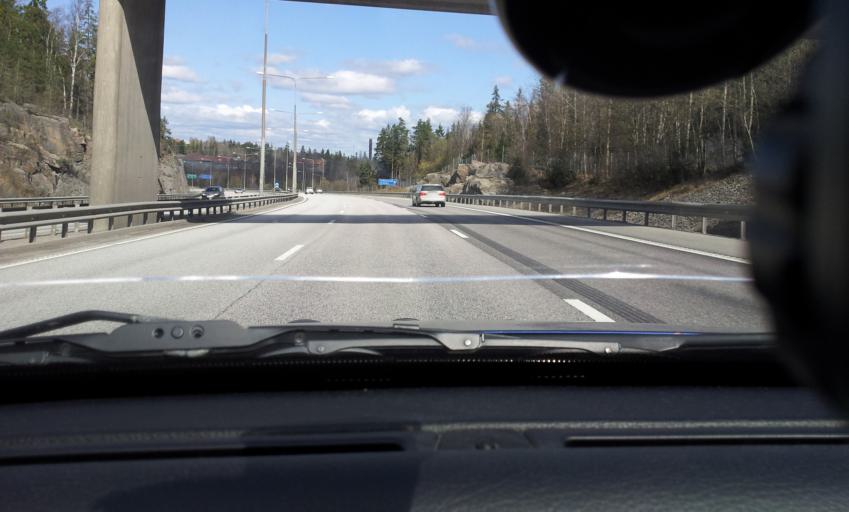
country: SE
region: Stockholm
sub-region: Haninge Kommun
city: Handen
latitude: 59.2145
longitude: 18.1339
